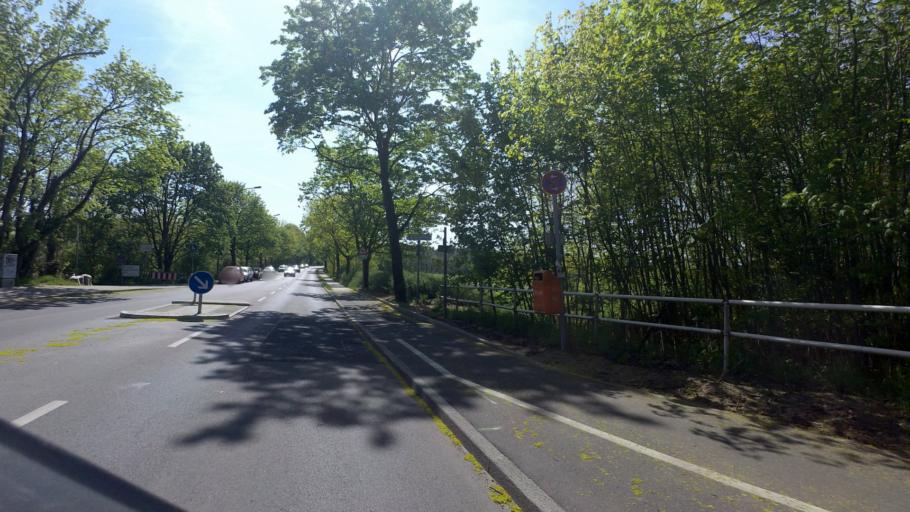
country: DE
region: Berlin
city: Gatow
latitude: 52.4790
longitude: 13.1793
